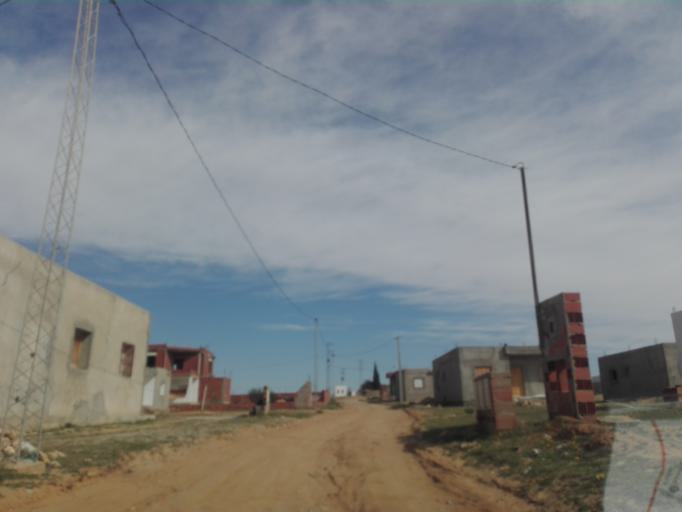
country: TN
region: Safaqis
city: Sfax
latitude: 34.7423
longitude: 10.5111
